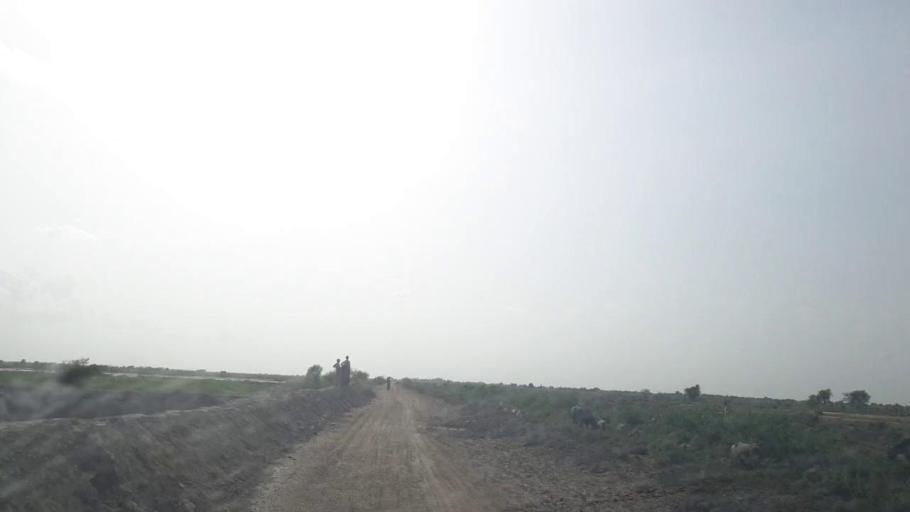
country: PK
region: Sindh
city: Tando Bago
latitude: 24.8129
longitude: 69.1542
